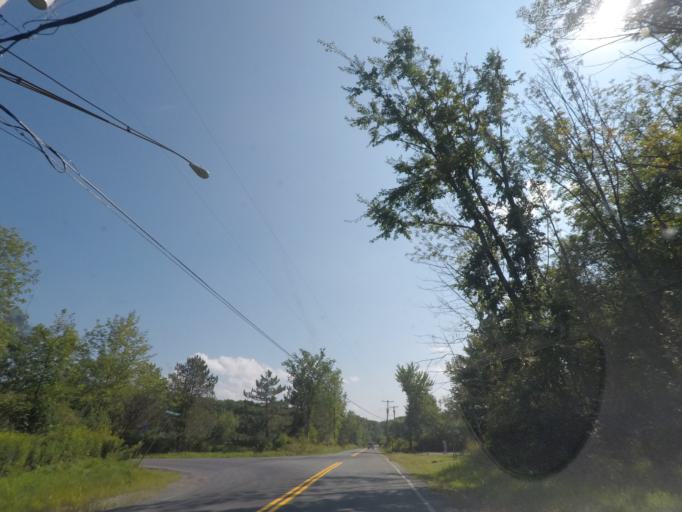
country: US
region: New York
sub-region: Rensselaer County
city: Poestenkill
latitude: 42.7335
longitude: -73.5096
